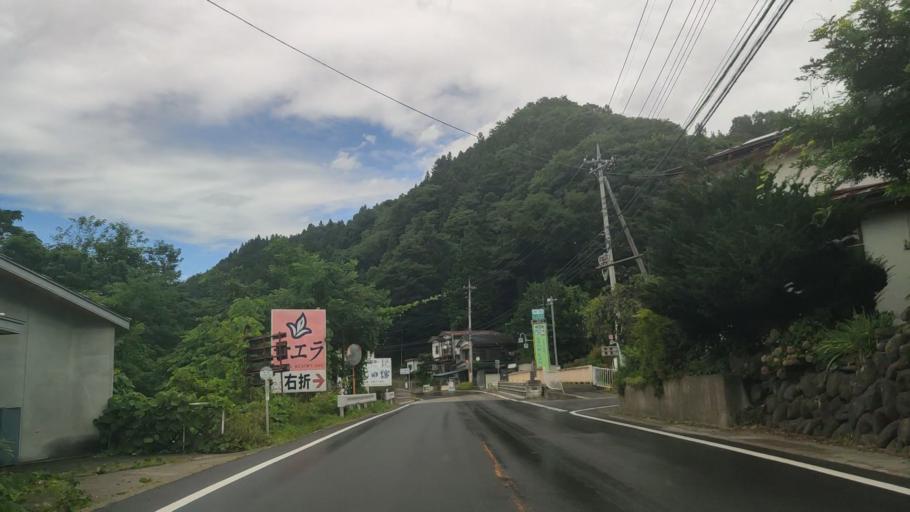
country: JP
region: Gunma
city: Numata
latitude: 36.7425
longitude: 139.2331
